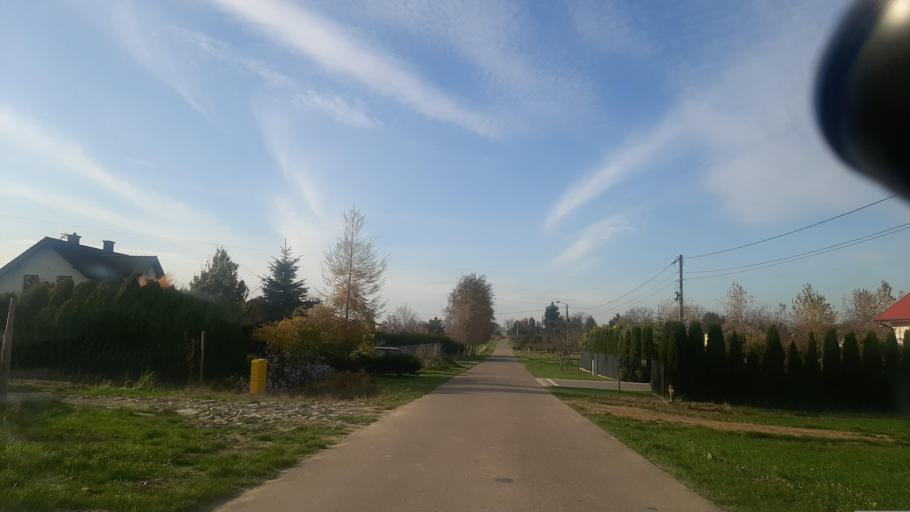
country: PL
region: Lublin Voivodeship
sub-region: Powiat pulawski
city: Markuszow
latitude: 51.3637
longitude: 22.2885
